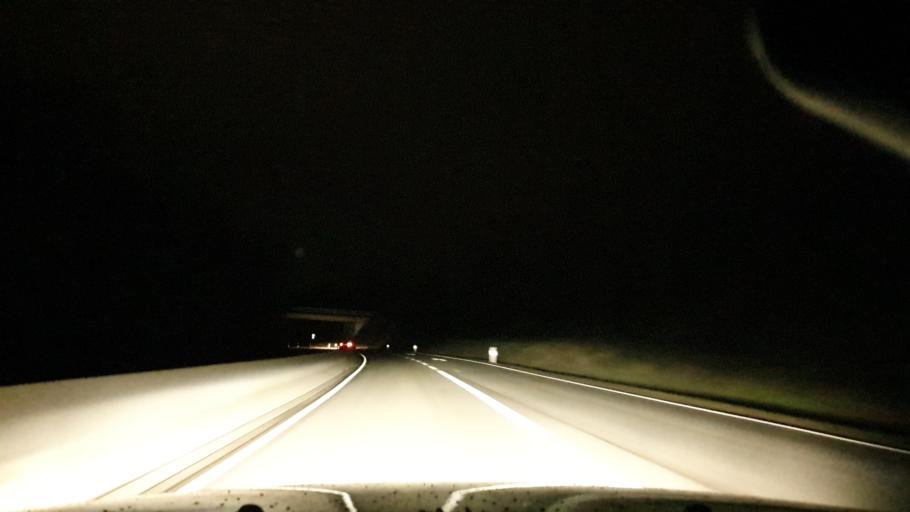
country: DE
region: Rheinland-Pfalz
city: Katzweiler
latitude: 49.4712
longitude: 7.6995
